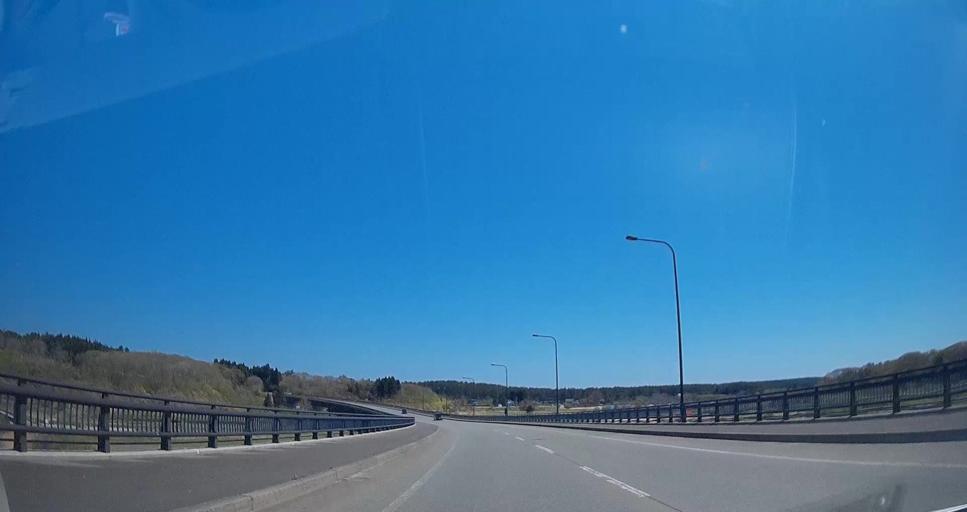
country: JP
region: Aomori
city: Misawa
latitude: 40.9815
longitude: 141.3607
